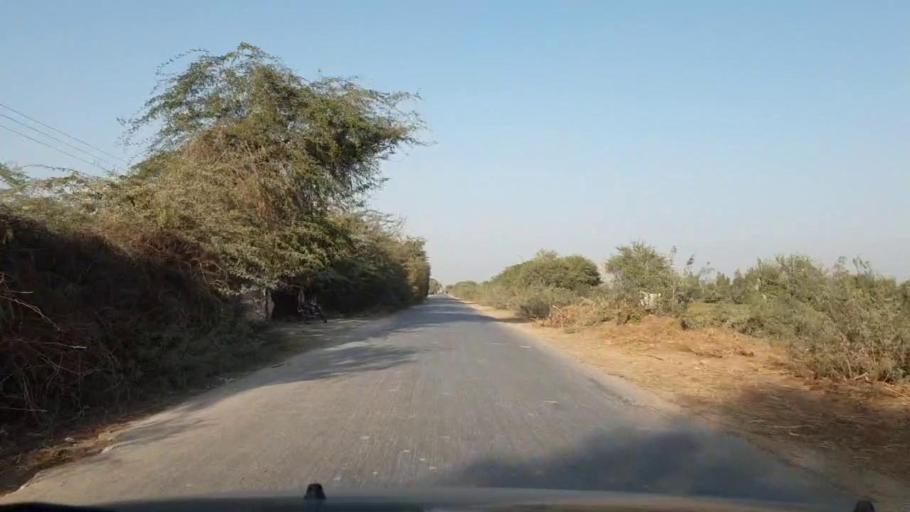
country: PK
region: Sindh
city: Chambar
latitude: 25.2646
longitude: 68.7997
